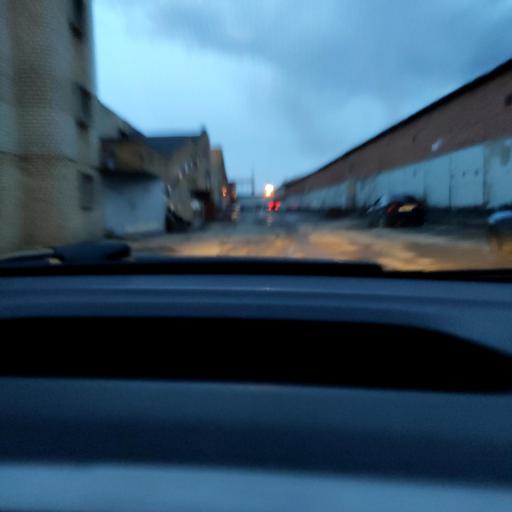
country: RU
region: Samara
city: Tol'yatti
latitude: 53.5419
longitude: 49.2675
